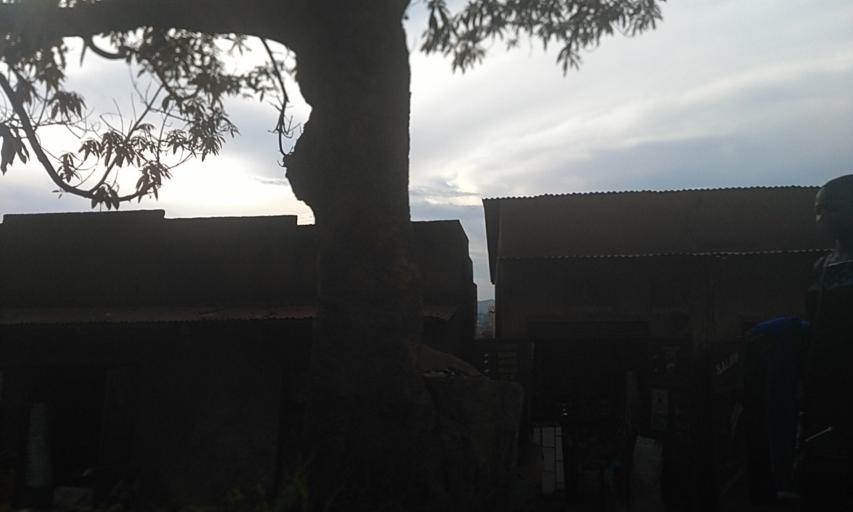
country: UG
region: Central Region
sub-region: Wakiso District
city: Kajansi
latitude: 0.2692
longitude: 32.5131
